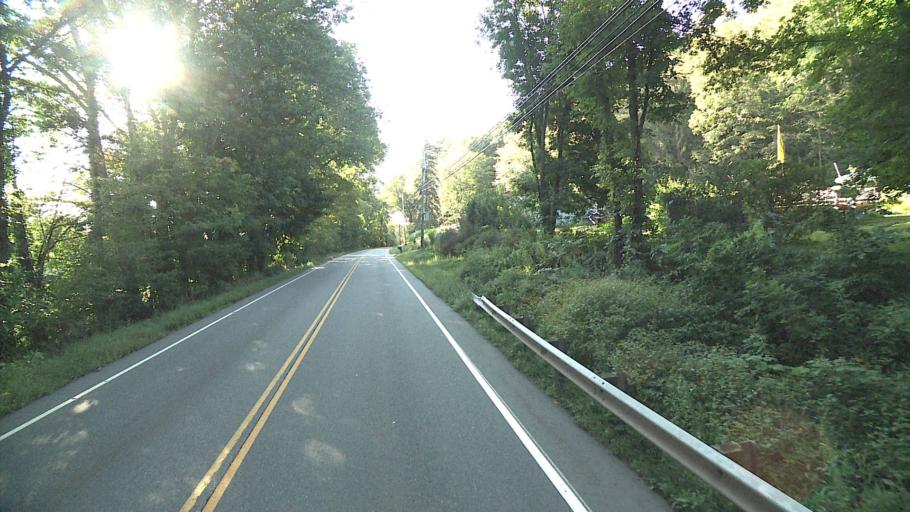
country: US
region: Connecticut
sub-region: New London County
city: Baltic
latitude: 41.6089
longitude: -72.1420
